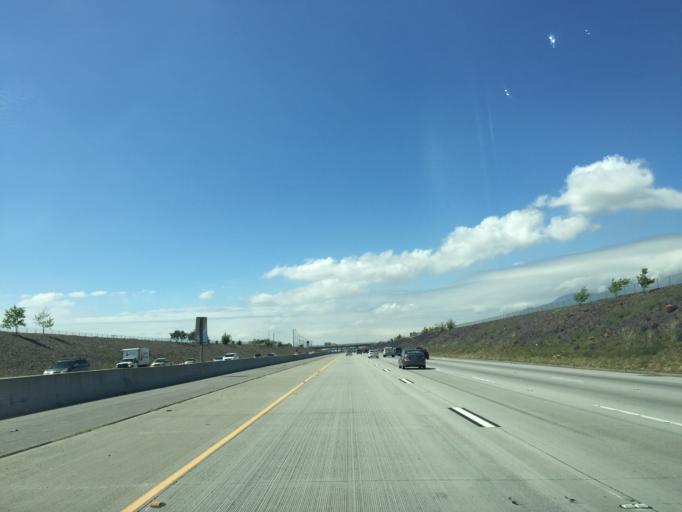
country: US
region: California
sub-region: San Bernardino County
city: Rialto
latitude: 34.1362
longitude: -117.4013
